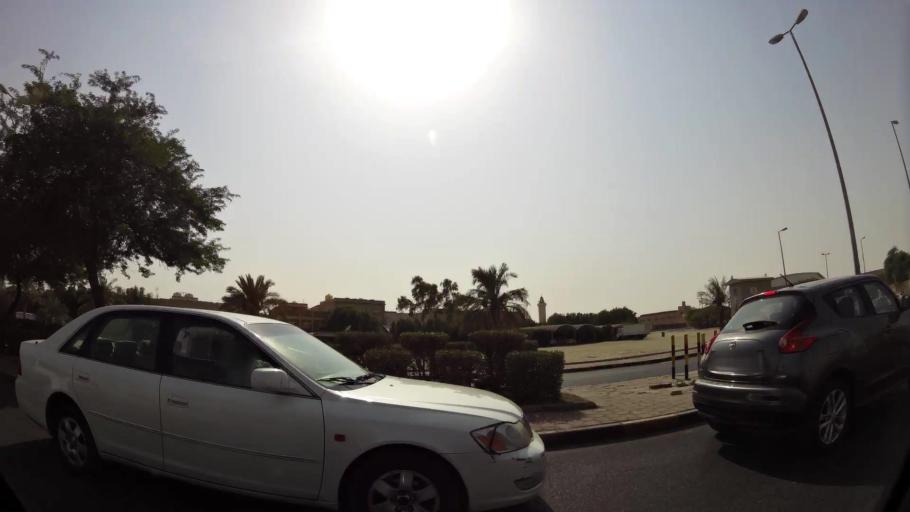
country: KW
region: Muhafazat al Jahra'
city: Al Jahra'
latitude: 29.3435
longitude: 47.6660
